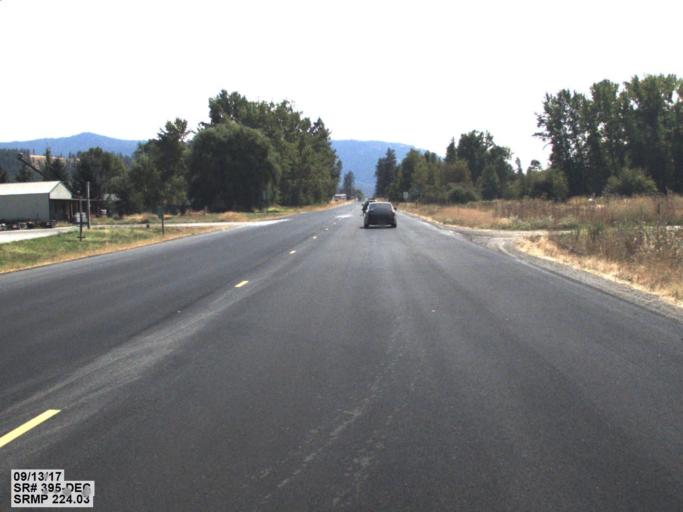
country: US
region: Washington
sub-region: Stevens County
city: Colville
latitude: 48.4688
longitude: -117.8887
